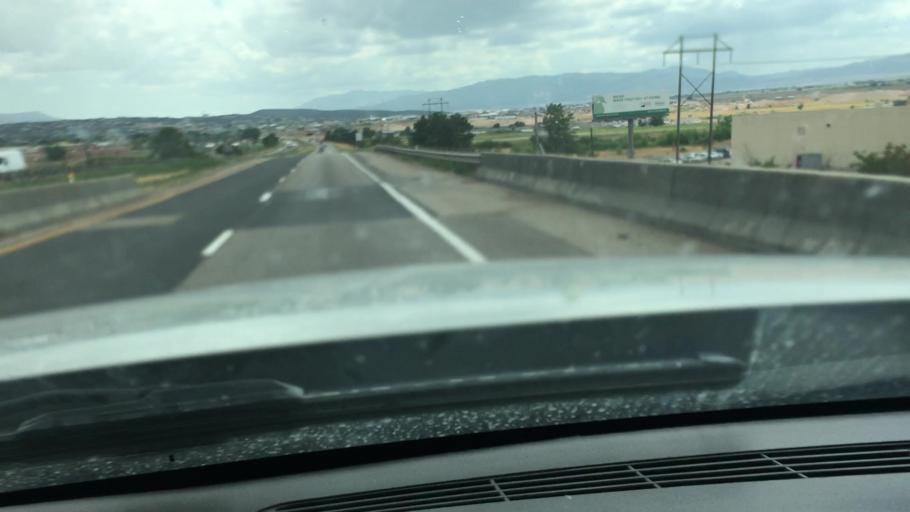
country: US
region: Utah
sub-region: Iron County
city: Cedar City
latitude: 37.7217
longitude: -113.0591
